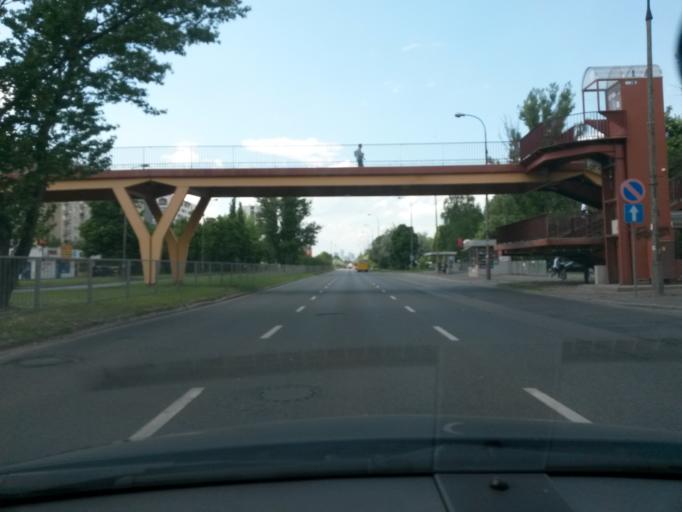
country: PL
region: Masovian Voivodeship
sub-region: Warszawa
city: Mokotow
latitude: 52.1853
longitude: 21.0523
